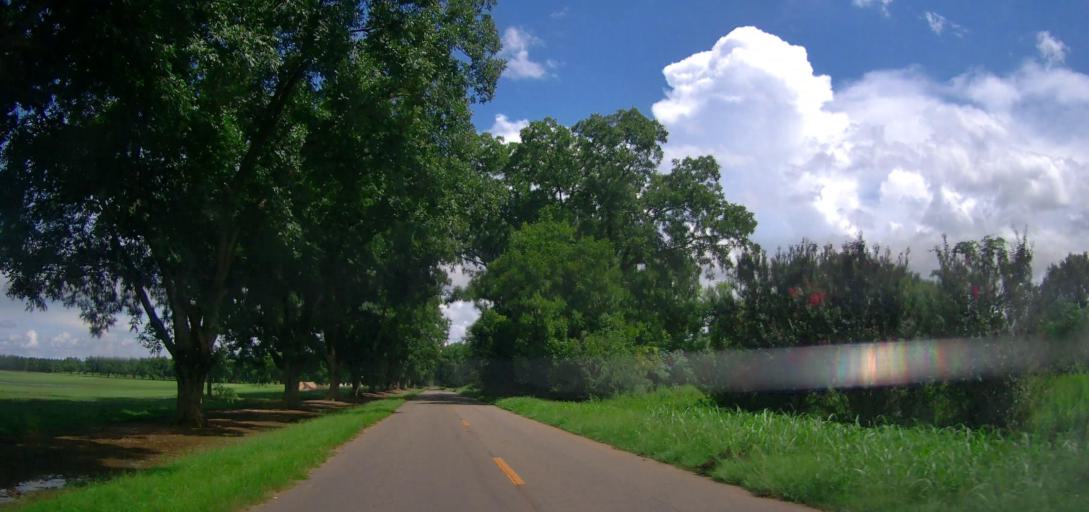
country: US
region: Georgia
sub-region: Macon County
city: Marshallville
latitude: 32.4485
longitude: -83.9870
